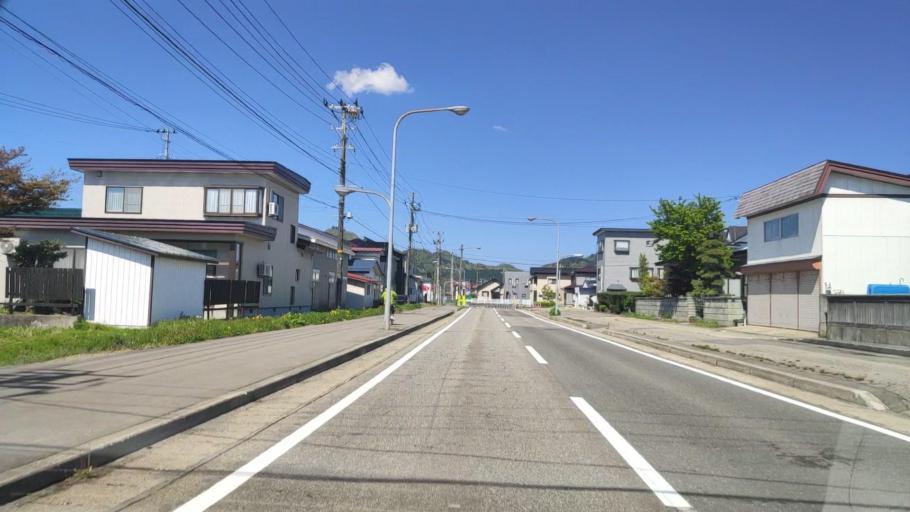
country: JP
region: Akita
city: Omagari
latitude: 39.4697
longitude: 140.4782
